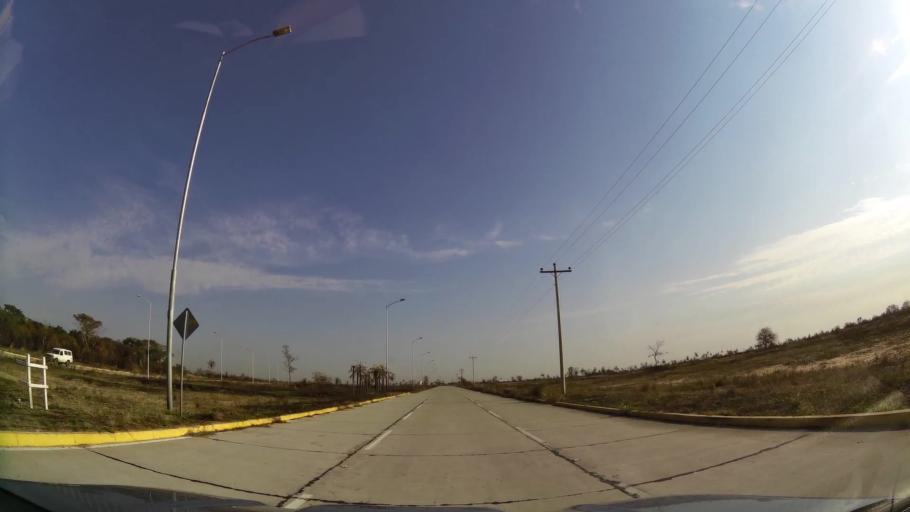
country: BO
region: Santa Cruz
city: Santa Cruz de la Sierra
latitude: -17.6684
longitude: -63.1294
